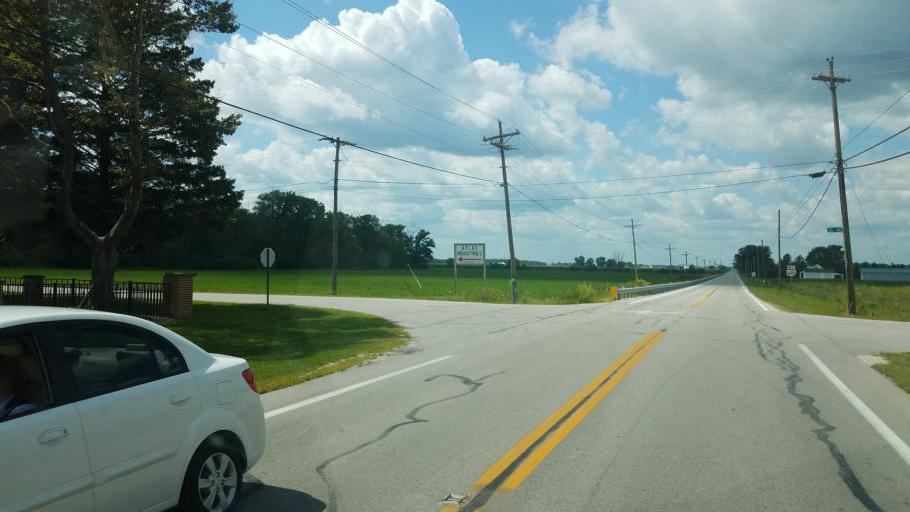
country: US
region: Ohio
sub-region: Sandusky County
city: Gibsonburg
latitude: 41.3845
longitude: -83.3387
